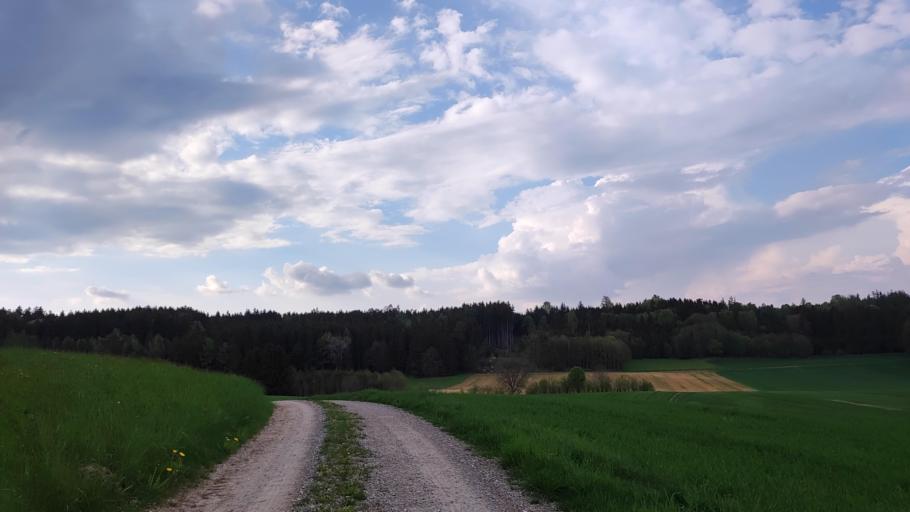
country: DE
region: Bavaria
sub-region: Swabia
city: Zusmarshausen
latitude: 48.3866
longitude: 10.5659
